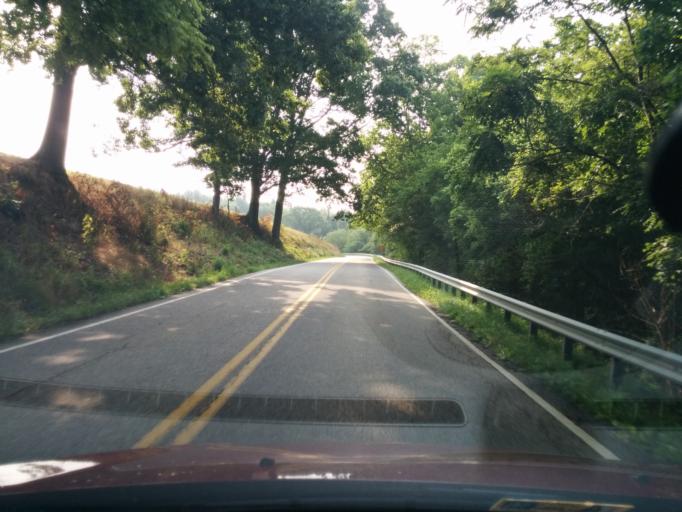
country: US
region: Virginia
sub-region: City of Lexington
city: Lexington
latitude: 37.7449
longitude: -79.5105
